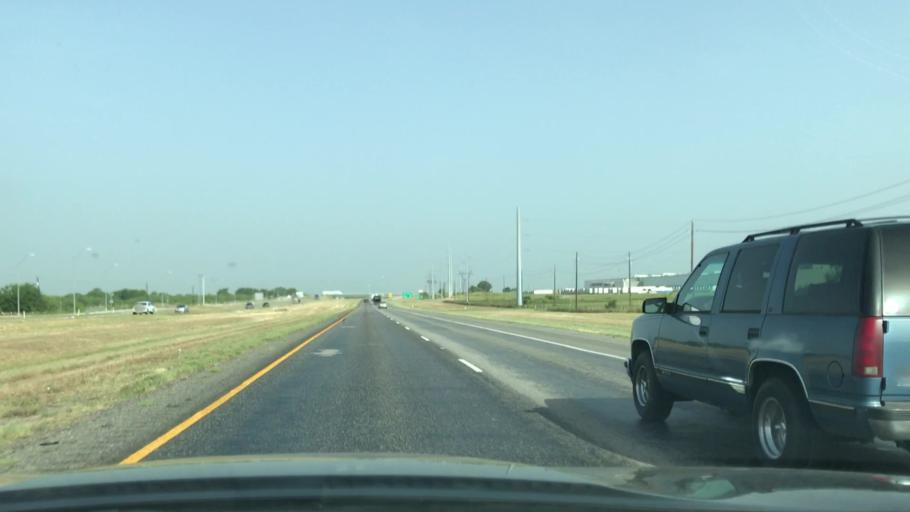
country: US
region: Texas
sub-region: Kaufman County
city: Terrell
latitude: 32.7257
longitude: -96.3304
